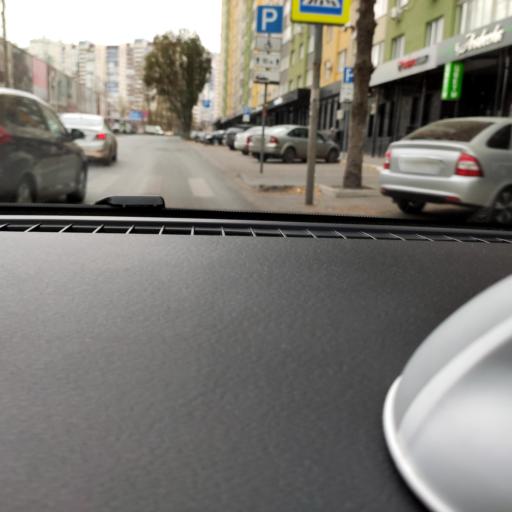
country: RU
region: Samara
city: Samara
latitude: 53.2074
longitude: 50.1761
